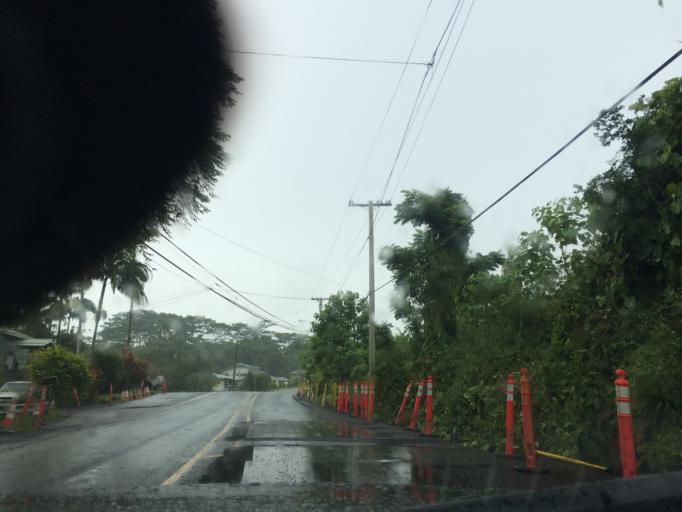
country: US
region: Hawaii
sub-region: Hawaii County
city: Hilo
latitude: 19.6960
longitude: -155.1185
